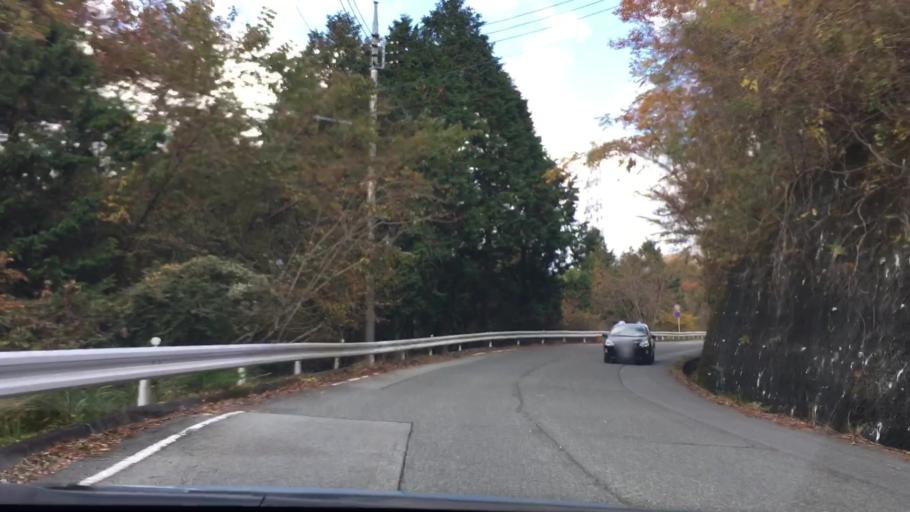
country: JP
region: Shizuoka
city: Gotemba
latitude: 35.3913
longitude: 138.9425
